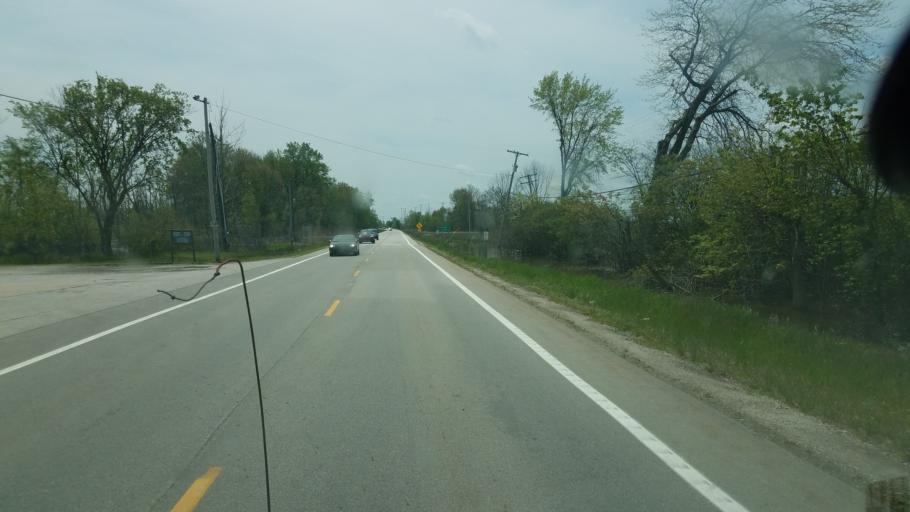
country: US
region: Ohio
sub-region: Ottawa County
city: Oak Harbor
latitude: 41.4580
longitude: -83.0514
